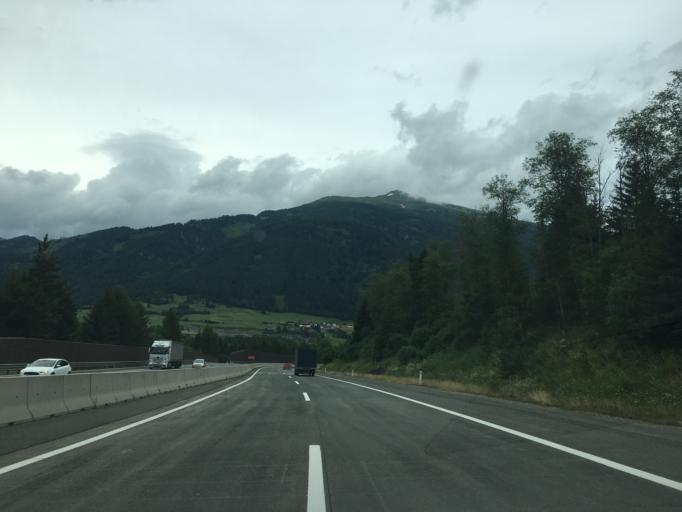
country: AT
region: Salzburg
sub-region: Politischer Bezirk Tamsweg
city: Sankt Michael im Lungau
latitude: 47.0861
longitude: 13.6068
